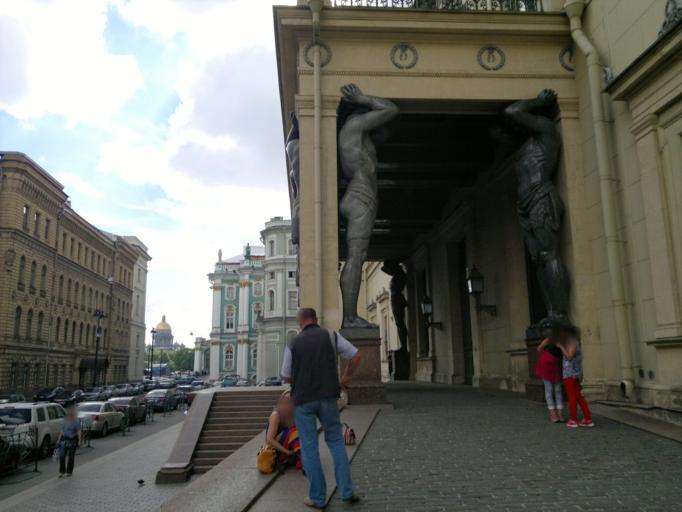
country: RU
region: St.-Petersburg
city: Saint Petersburg
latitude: 59.9412
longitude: 30.3180
